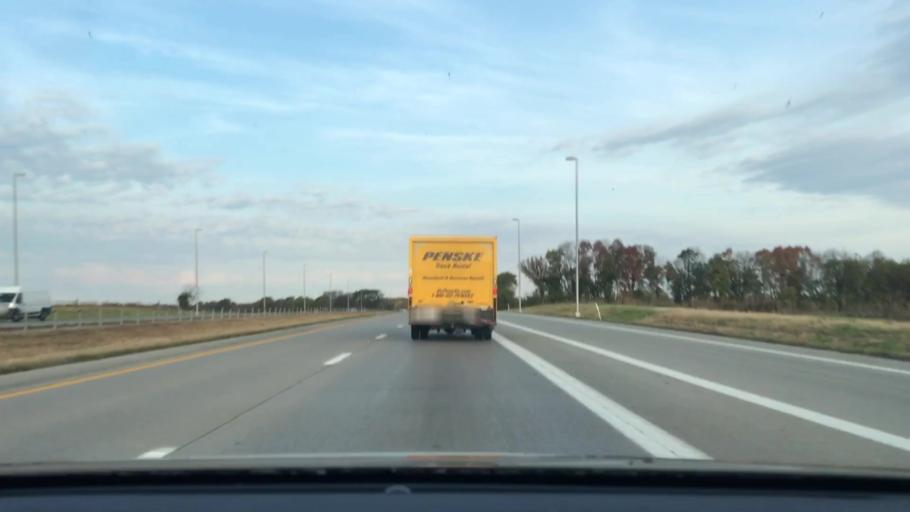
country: US
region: Kentucky
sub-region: Christian County
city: Fort Campbell North
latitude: 36.7463
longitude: -87.5146
